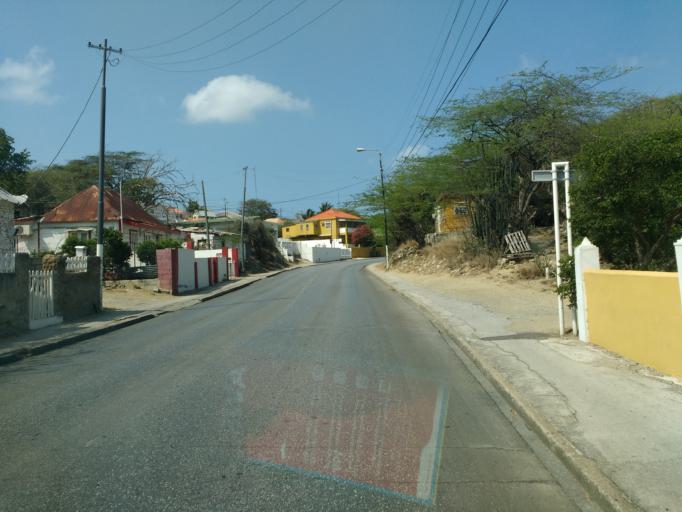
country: CW
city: Willemstad
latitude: 12.1050
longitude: -68.9150
